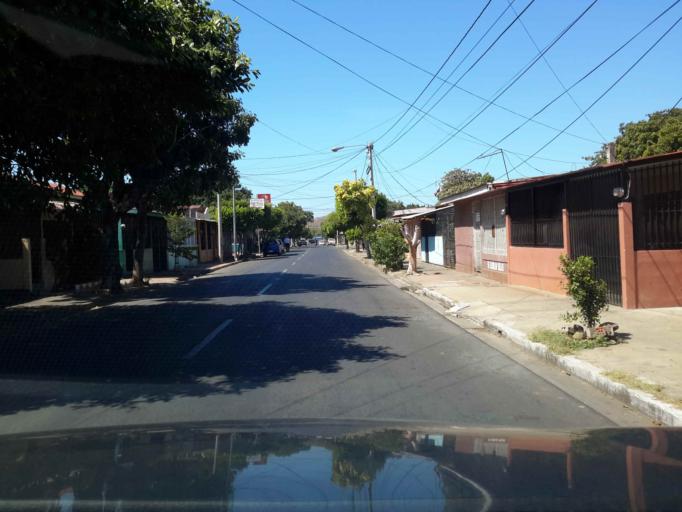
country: NI
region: Managua
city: Ciudad Sandino
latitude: 12.1504
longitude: -86.3011
